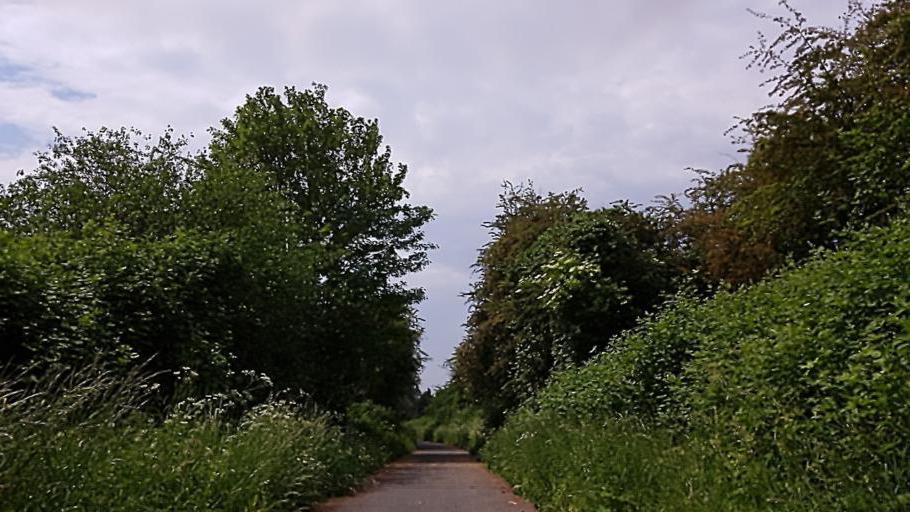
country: BE
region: Wallonia
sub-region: Province du Hainaut
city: Peruwelz
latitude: 50.5133
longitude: 3.5827
